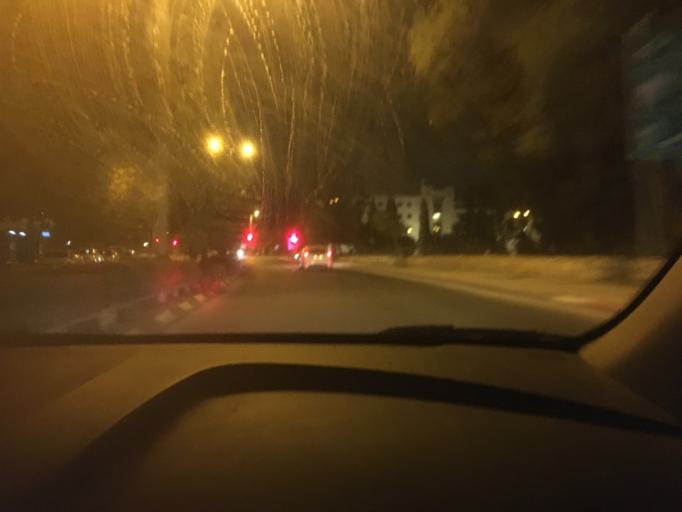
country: IL
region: Jerusalem
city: Jerusalem
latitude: 31.7569
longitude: 35.2249
